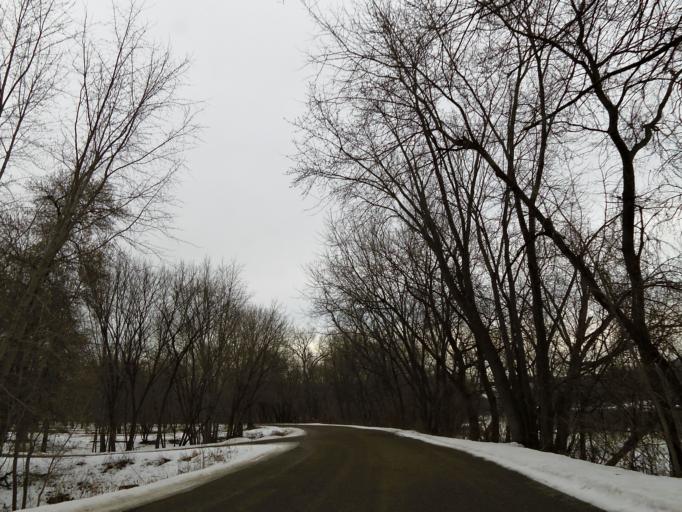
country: US
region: Minnesota
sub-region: Dakota County
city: Mendota Heights
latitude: 44.8800
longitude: -93.1800
